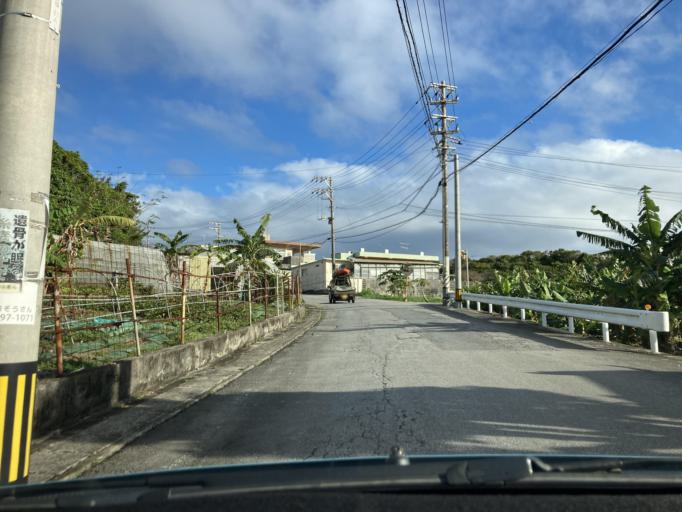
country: JP
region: Okinawa
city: Itoman
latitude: 26.1161
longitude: 127.6738
